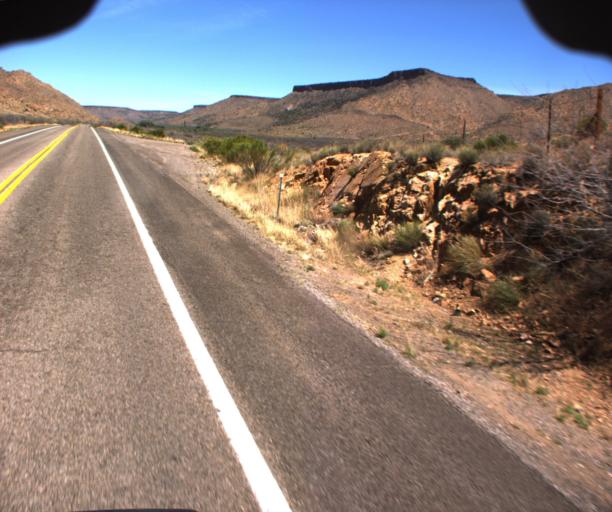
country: US
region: Arizona
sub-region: Mohave County
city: Peach Springs
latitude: 35.3712
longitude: -113.6699
